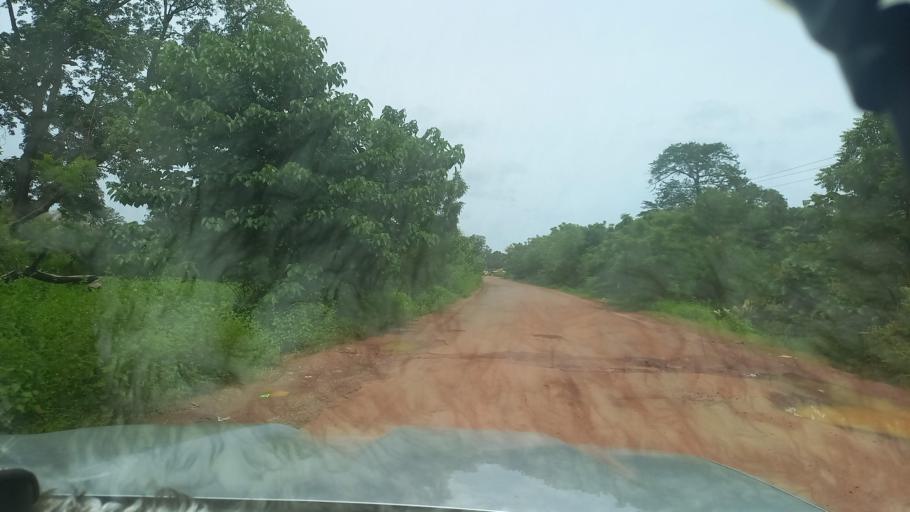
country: SN
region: Kolda
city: Marsassoum
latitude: 12.9122
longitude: -16.0108
